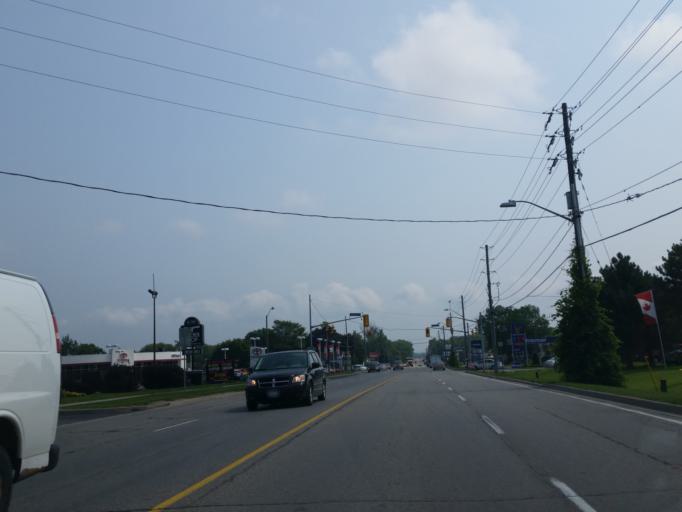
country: CA
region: Ontario
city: Brockville
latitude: 44.6046
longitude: -75.7164
